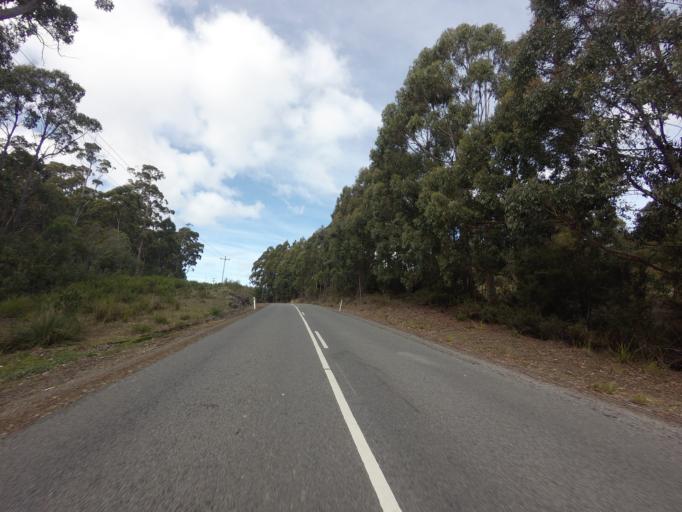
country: AU
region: Tasmania
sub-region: Clarence
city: Sandford
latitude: -43.1390
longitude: 147.8158
